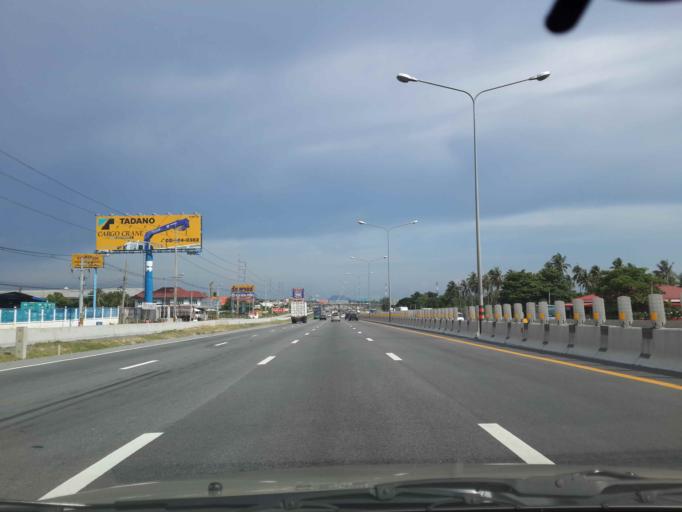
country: TH
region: Chon Buri
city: Si Racha
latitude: 13.2446
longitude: 100.9955
